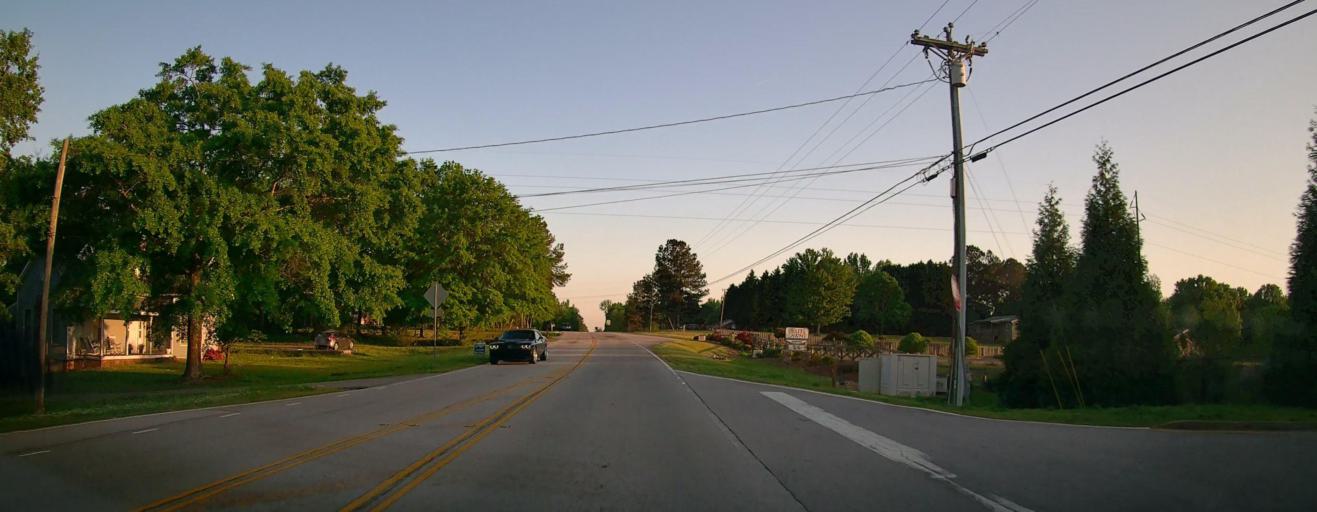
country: US
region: Georgia
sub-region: Henry County
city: McDonough
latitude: 33.4278
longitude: -84.0906
